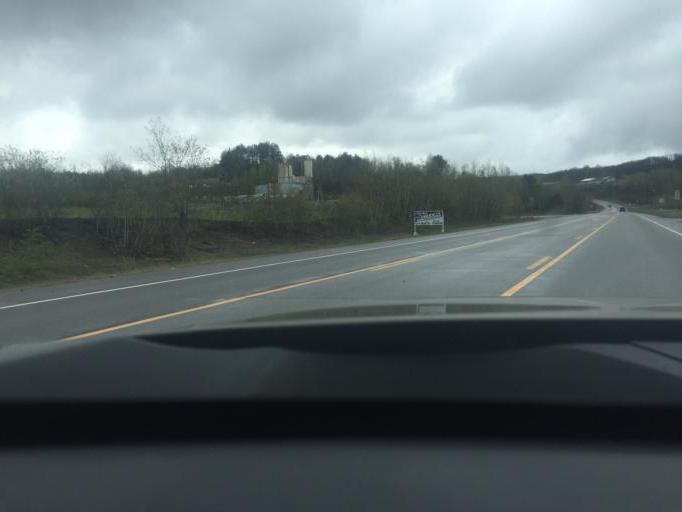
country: US
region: Pennsylvania
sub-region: Luzerne County
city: Harleigh
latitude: 40.9923
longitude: -75.9903
